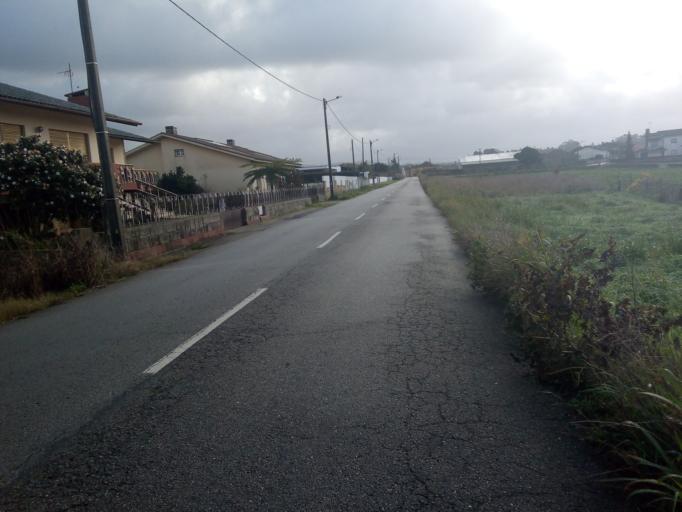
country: PT
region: Aveiro
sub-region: Estarreja
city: Beduido
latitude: 40.7665
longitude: -8.5408
